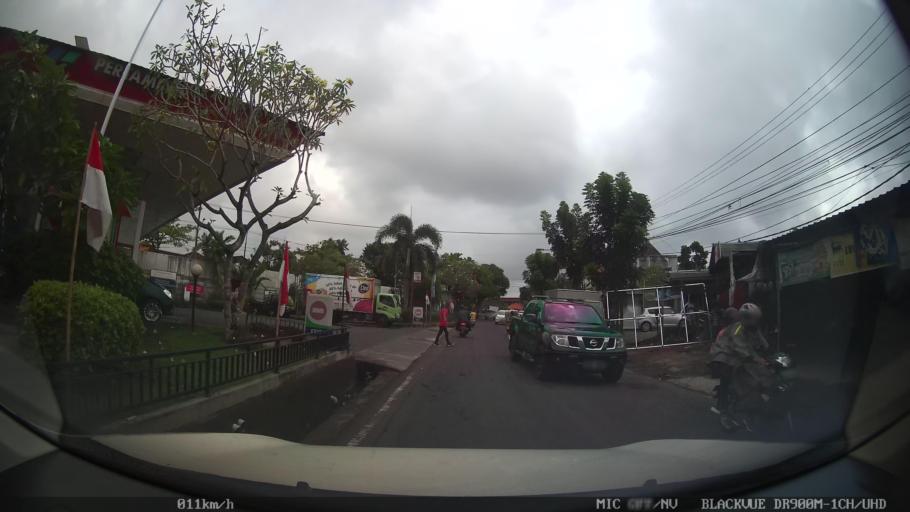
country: ID
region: Bali
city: Banjar Mambalkajanan
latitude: -8.5448
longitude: 115.2145
